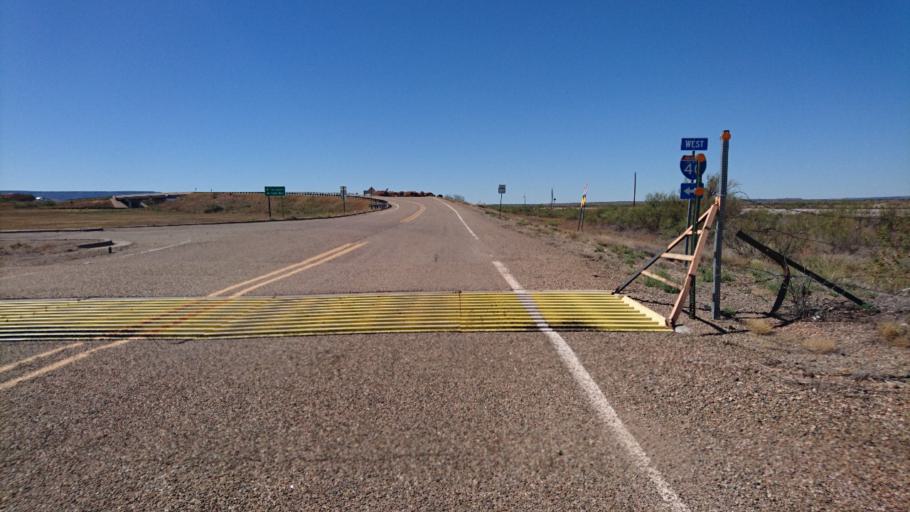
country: US
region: New Mexico
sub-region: Quay County
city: Tucumcari
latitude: 35.0952
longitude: -104.0680
